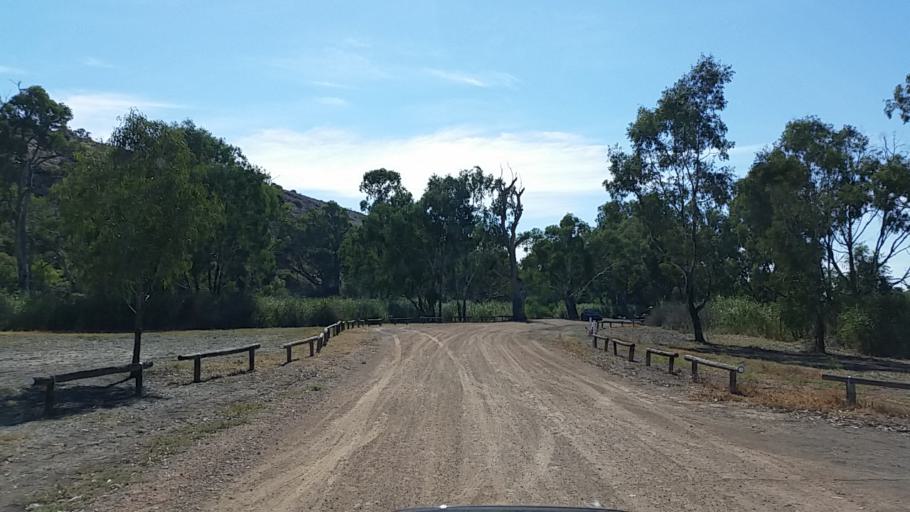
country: AU
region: South Australia
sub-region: Mid Murray
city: Mannum
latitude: -34.7003
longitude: 139.5760
